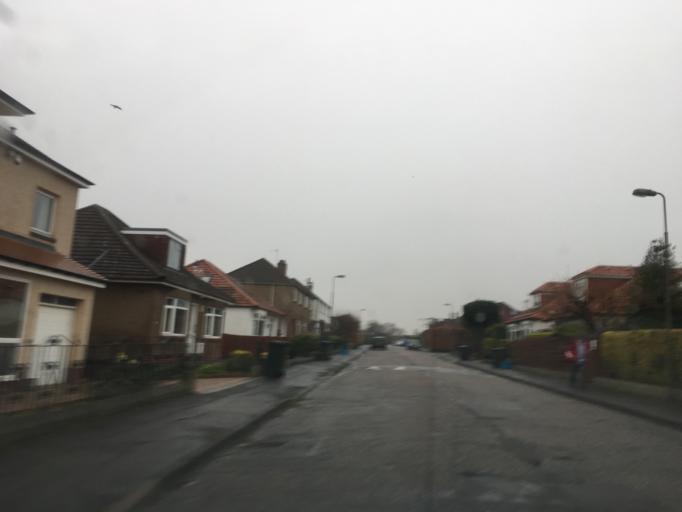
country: GB
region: Scotland
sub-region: Edinburgh
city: Currie
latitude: 55.9487
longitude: -3.3005
